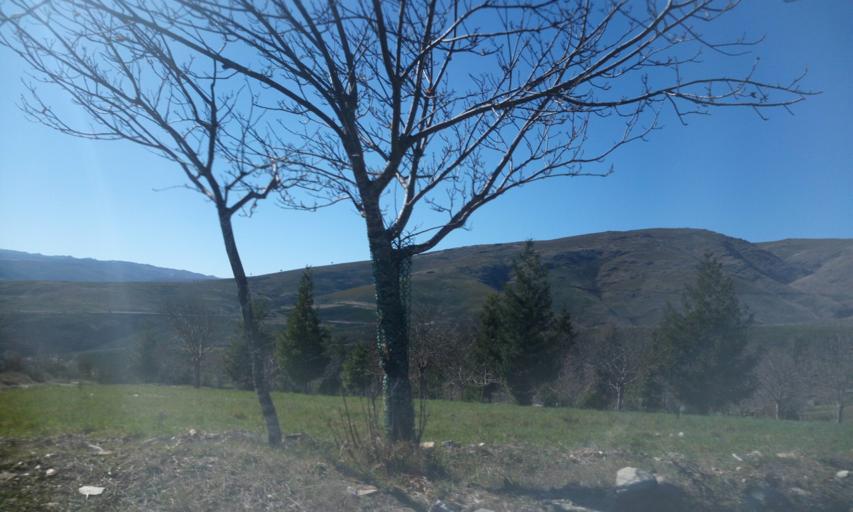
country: PT
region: Guarda
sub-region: Manteigas
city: Manteigas
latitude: 40.4693
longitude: -7.5029
